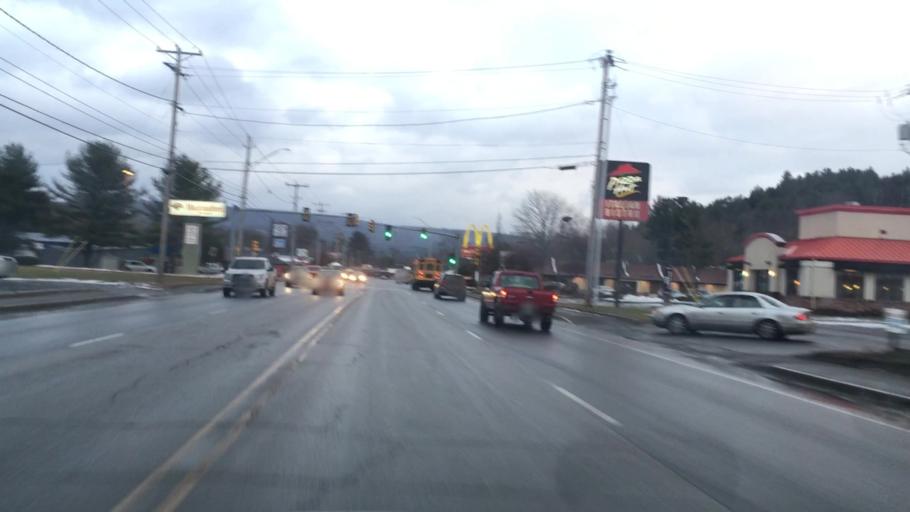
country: US
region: New Hampshire
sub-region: Sullivan County
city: Claremont
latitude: 43.3700
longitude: -72.3261
